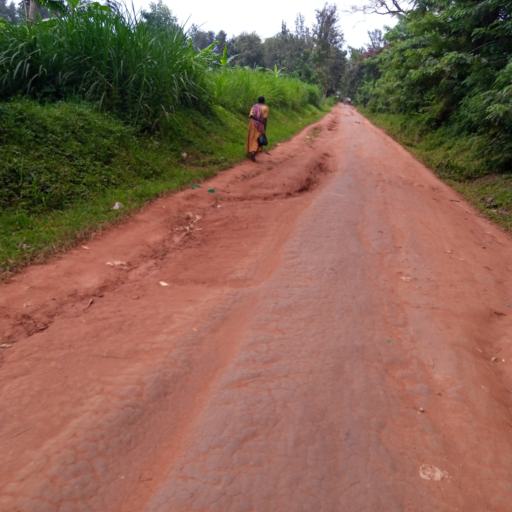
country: UG
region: Eastern Region
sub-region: Mbale District
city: Mbale
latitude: 1.0910
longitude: 34.1862
